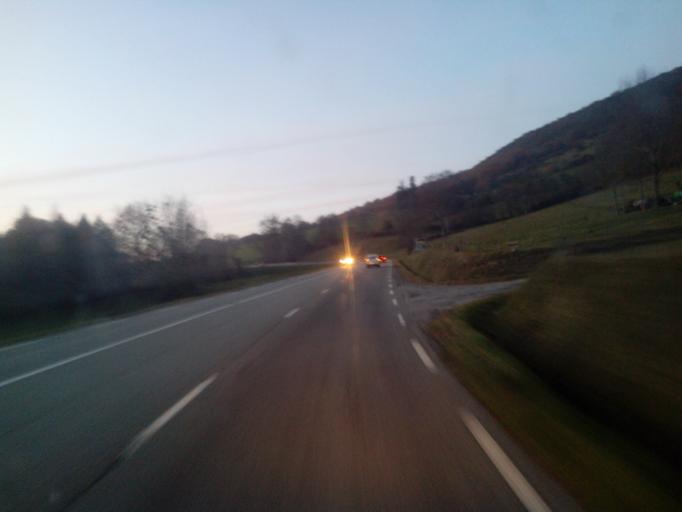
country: FR
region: Midi-Pyrenees
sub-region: Departement de l'Ariege
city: Foix
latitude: 42.9703
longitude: 1.5860
